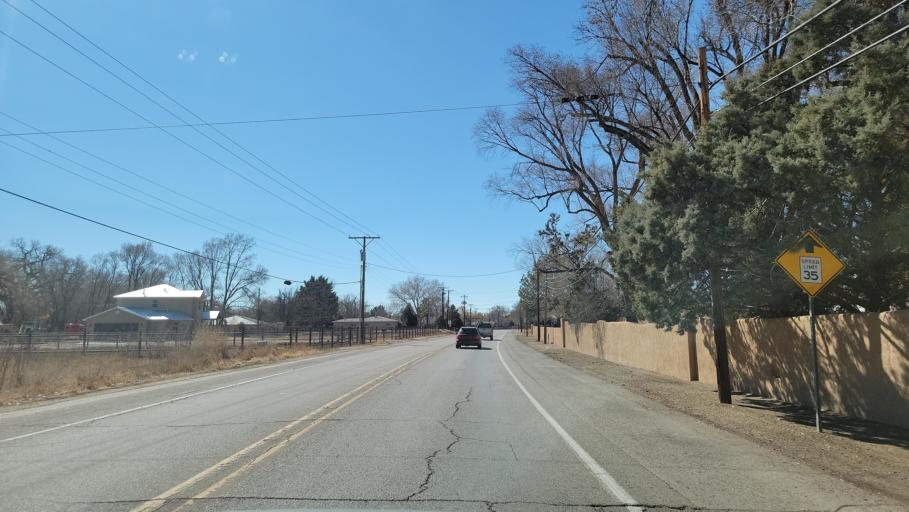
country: US
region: New Mexico
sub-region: Bernalillo County
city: South Valley
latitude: 35.0005
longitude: -106.6915
